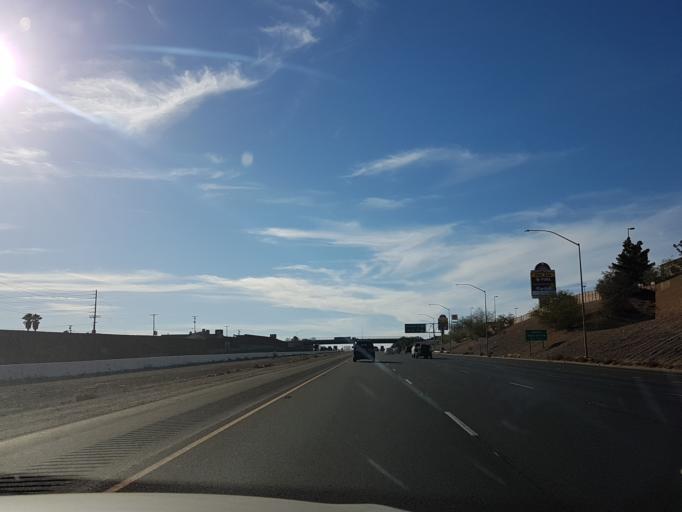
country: US
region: California
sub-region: San Bernardino County
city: Barstow
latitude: 34.8860
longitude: -117.0166
